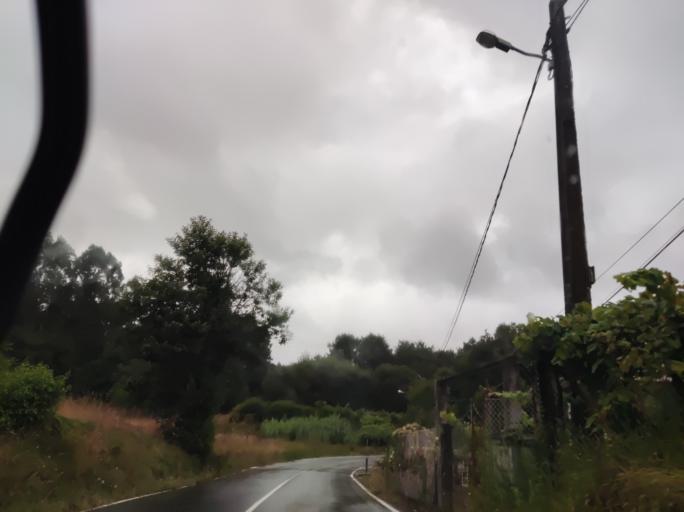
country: ES
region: Galicia
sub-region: Provincia da Coruna
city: Rianxo
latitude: 42.6954
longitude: -8.8409
